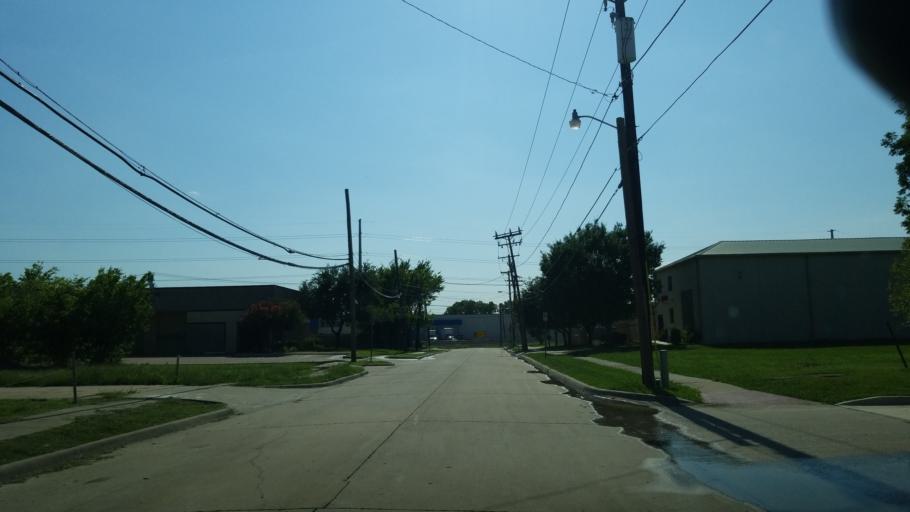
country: US
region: Texas
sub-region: Dallas County
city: Farmers Branch
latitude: 32.9293
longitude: -96.8970
